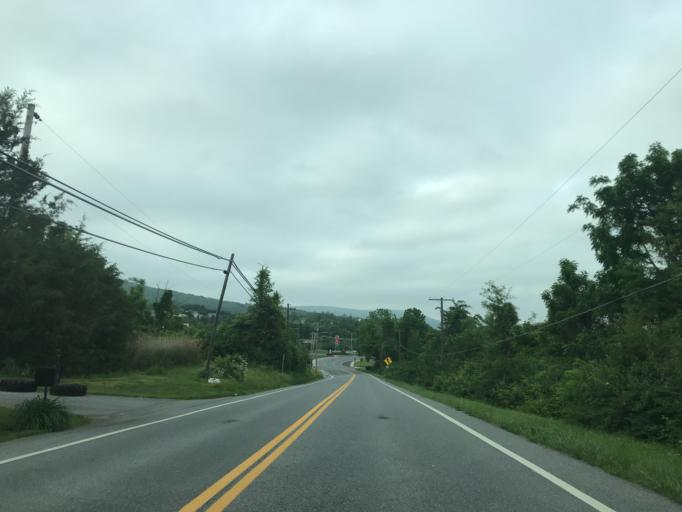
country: US
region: Maryland
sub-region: Frederick County
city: Thurmont
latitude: 39.6111
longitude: -77.4193
